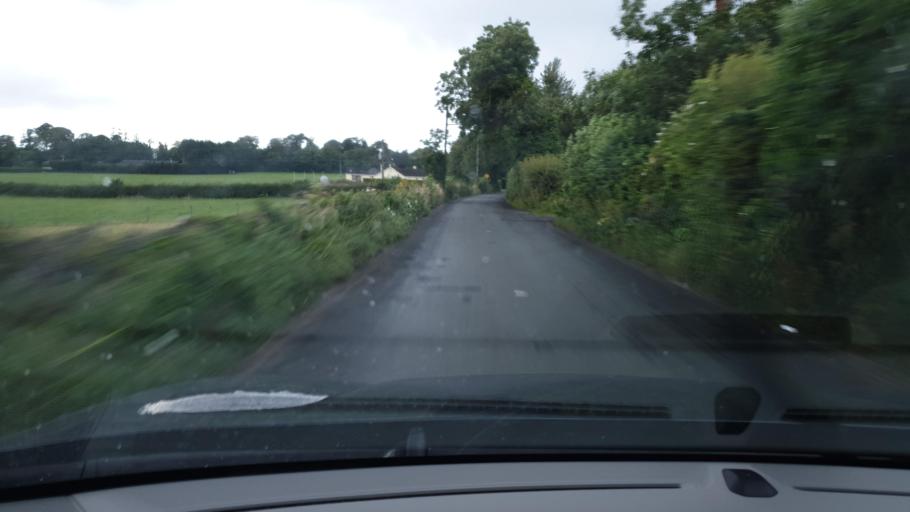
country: IE
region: Leinster
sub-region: South Dublin
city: Rathcoole
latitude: 53.2501
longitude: -6.5062
